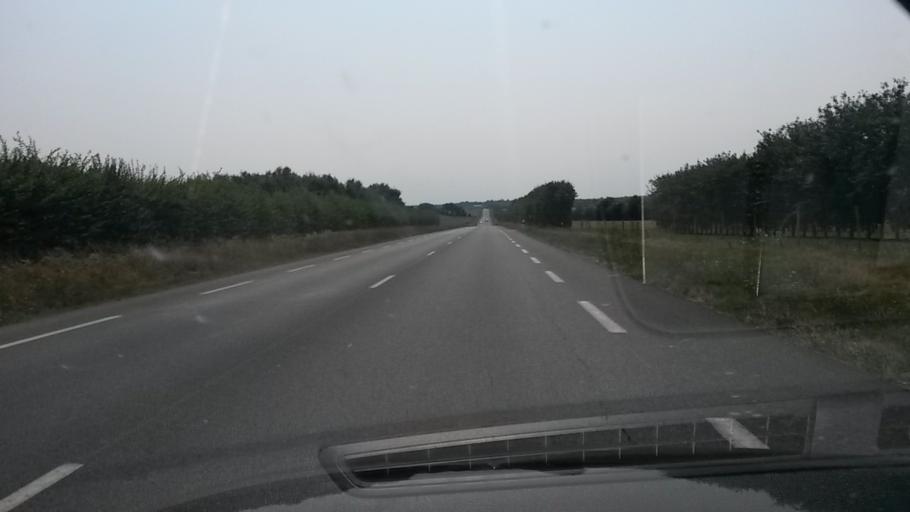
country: FR
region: Pays de la Loire
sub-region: Departement de la Mayenne
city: Chemaze
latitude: 47.7738
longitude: -0.7805
